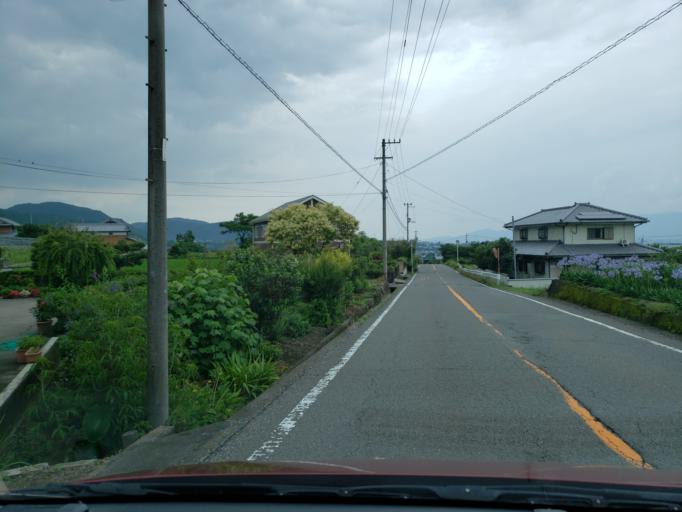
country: JP
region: Tokushima
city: Kamojimacho-jogejima
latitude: 34.1056
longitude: 134.2605
